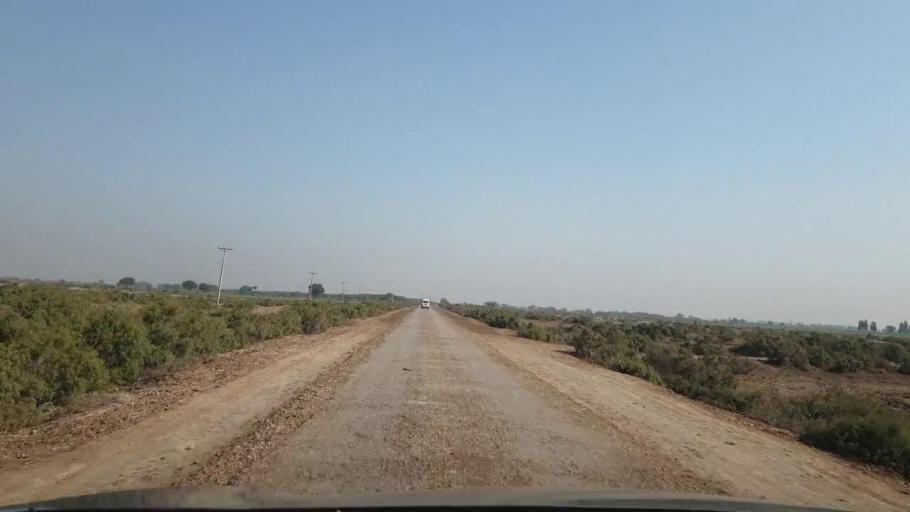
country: PK
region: Sindh
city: Berani
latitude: 25.6252
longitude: 68.8573
